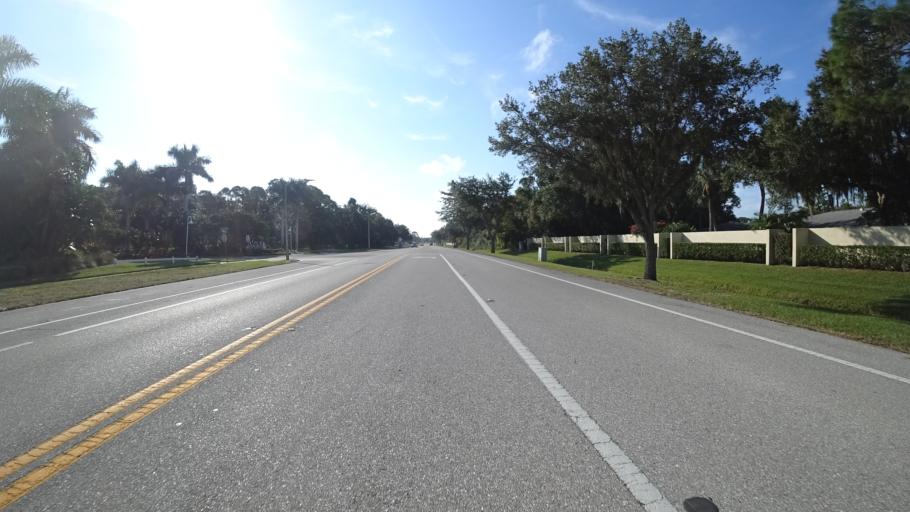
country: US
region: Florida
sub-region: Sarasota County
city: Desoto Lakes
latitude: 27.4149
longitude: -82.4909
